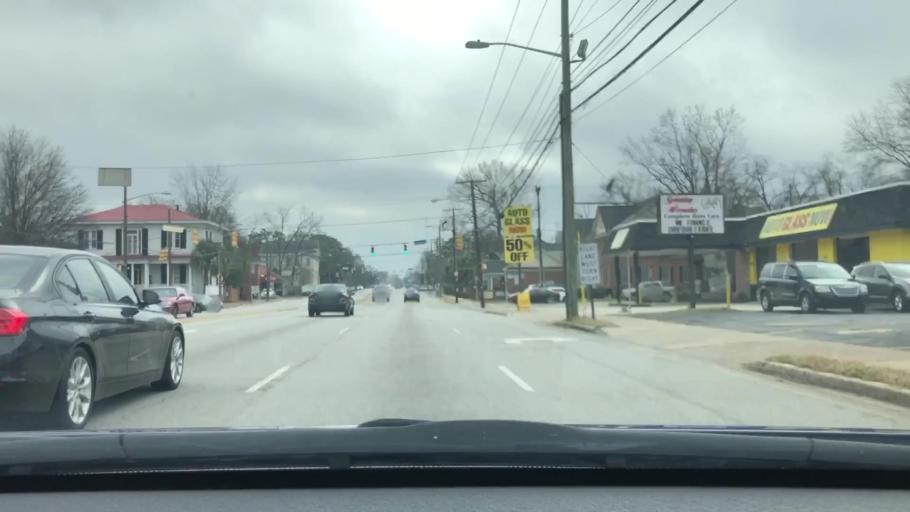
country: US
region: South Carolina
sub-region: Richland County
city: Columbia
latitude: 34.0140
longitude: -81.0338
